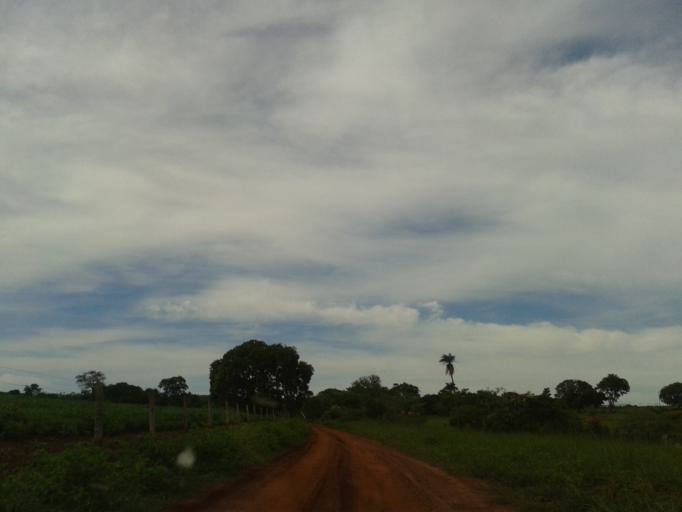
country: BR
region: Minas Gerais
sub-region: Capinopolis
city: Capinopolis
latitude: -18.7871
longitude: -49.8025
